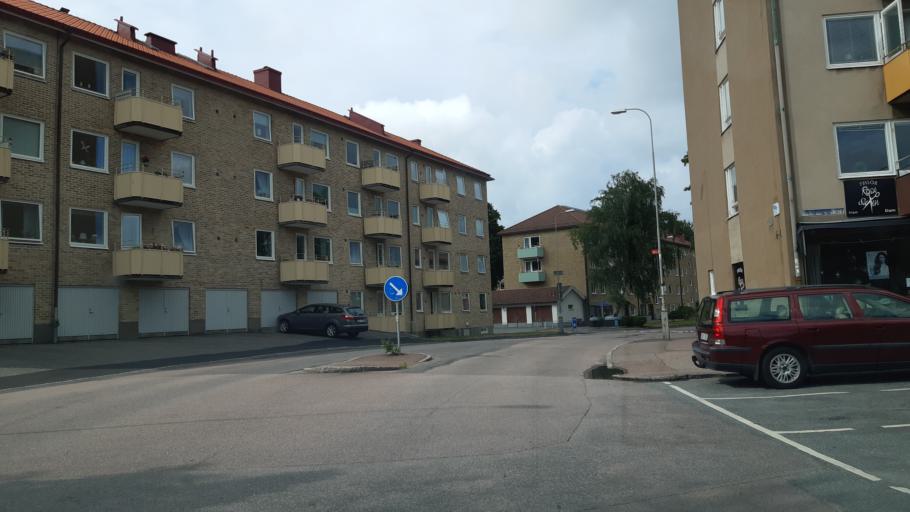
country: SE
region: Vaestra Goetaland
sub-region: Goteborg
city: Eriksbo
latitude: 57.7150
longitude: 12.0469
